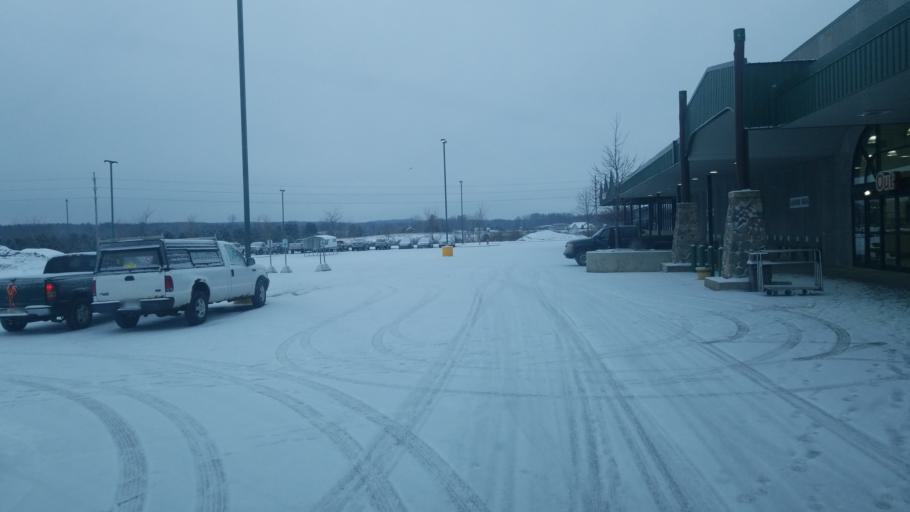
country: US
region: Michigan
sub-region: Mecosta County
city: Big Rapids
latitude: 43.6833
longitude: -85.5171
